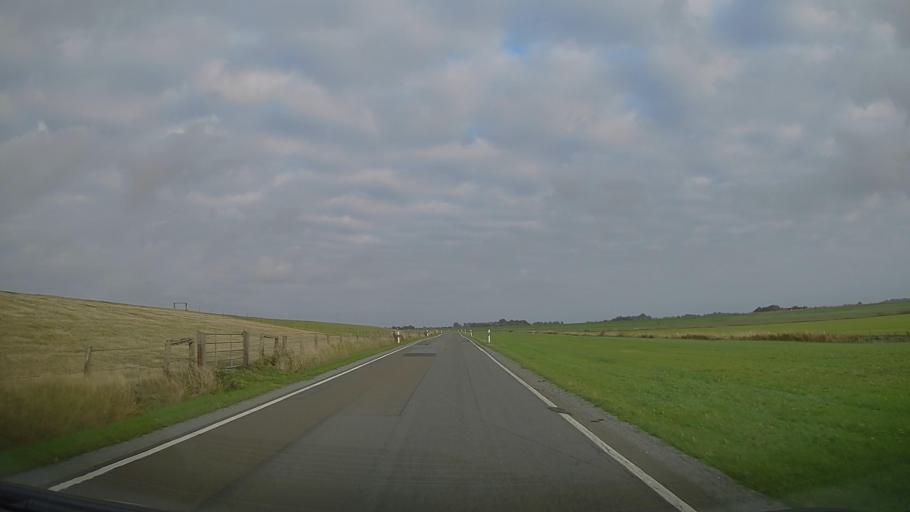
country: DE
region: Schleswig-Holstein
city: Tetenbull
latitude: 54.4031
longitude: 8.8485
